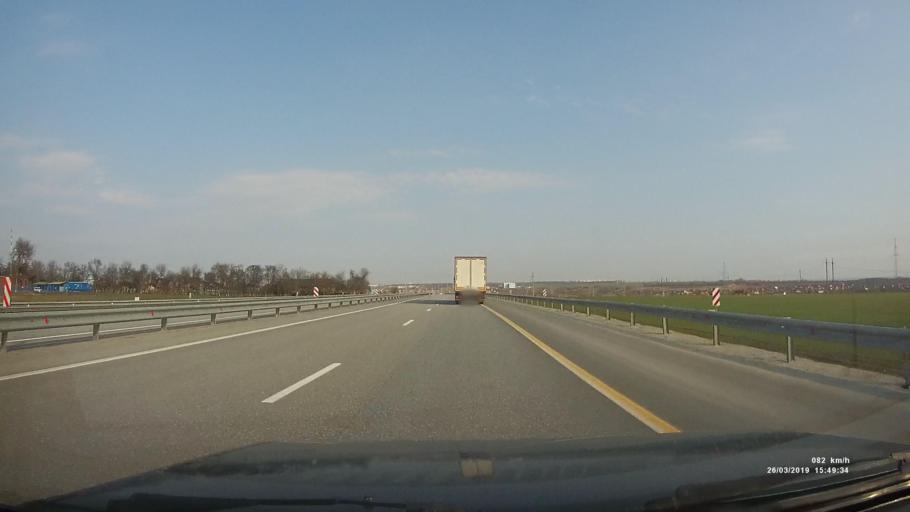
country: RU
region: Rostov
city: Chaltyr
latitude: 47.2755
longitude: 39.4716
